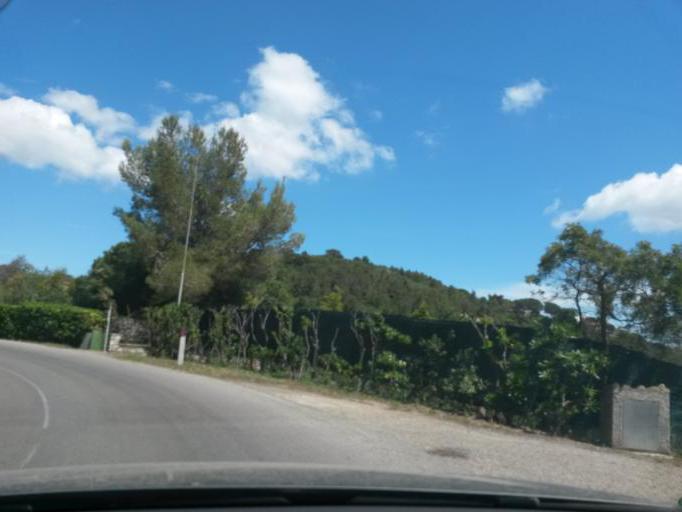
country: IT
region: Tuscany
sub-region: Provincia di Livorno
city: Capoliveri
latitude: 42.7683
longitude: 10.3413
